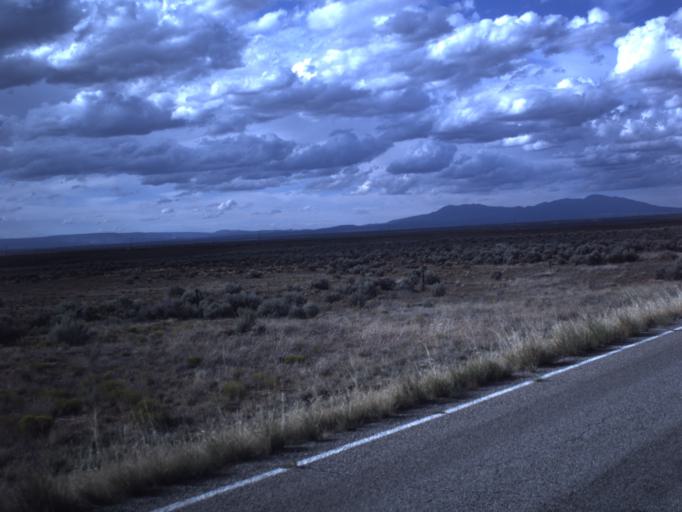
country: US
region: Utah
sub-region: San Juan County
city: Blanding
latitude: 37.3842
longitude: -109.3407
